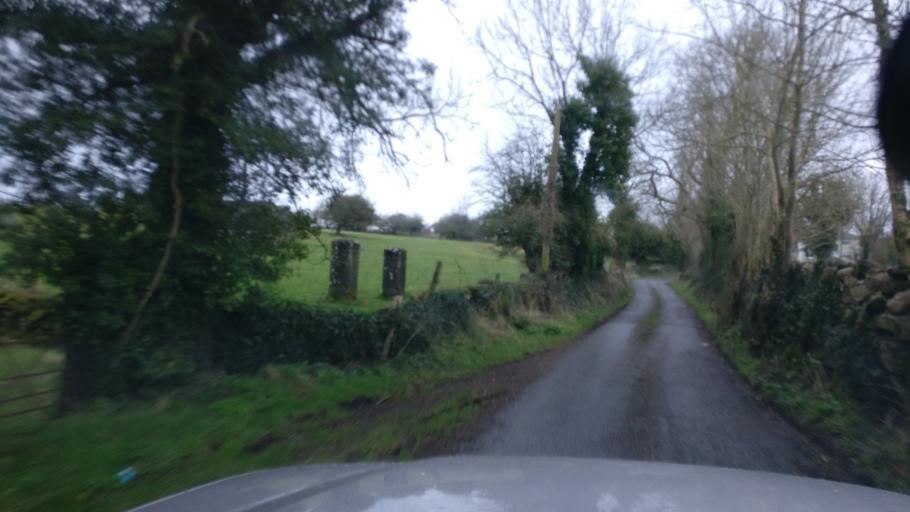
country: IE
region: Connaught
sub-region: County Galway
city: Loughrea
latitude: 53.1816
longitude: -8.6061
